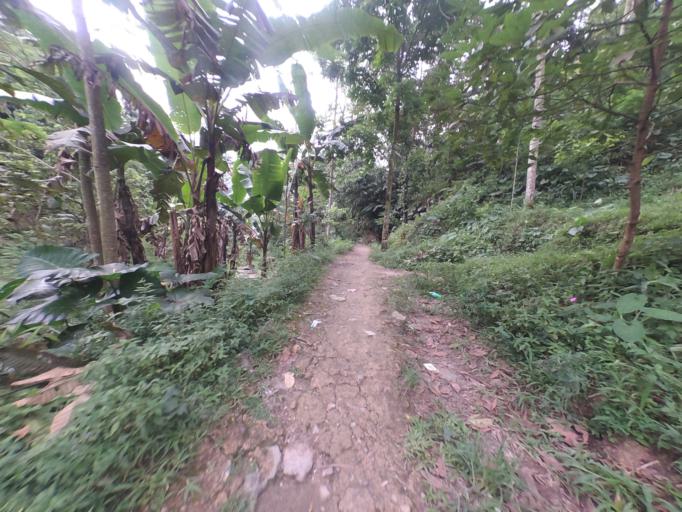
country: ID
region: West Java
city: Cicurug
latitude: -6.7072
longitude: 106.6643
